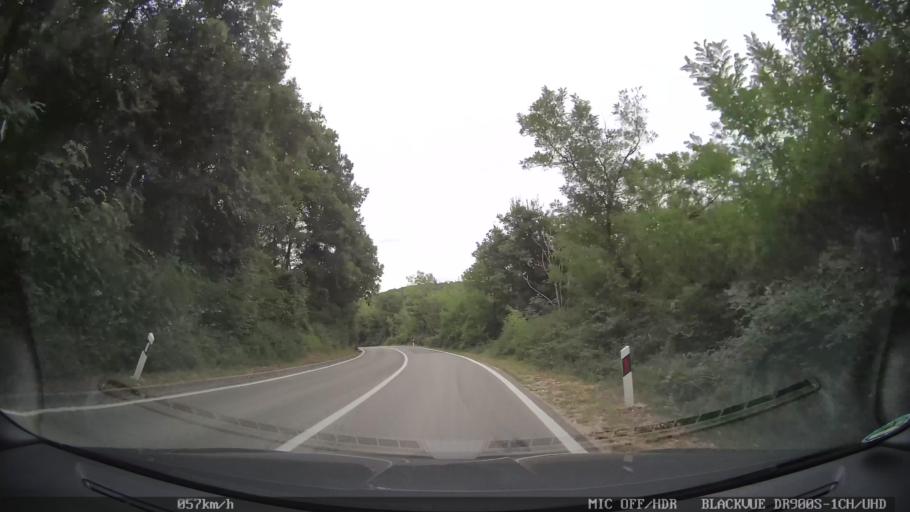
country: HR
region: Primorsko-Goranska
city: Punat
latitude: 45.0180
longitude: 14.6918
